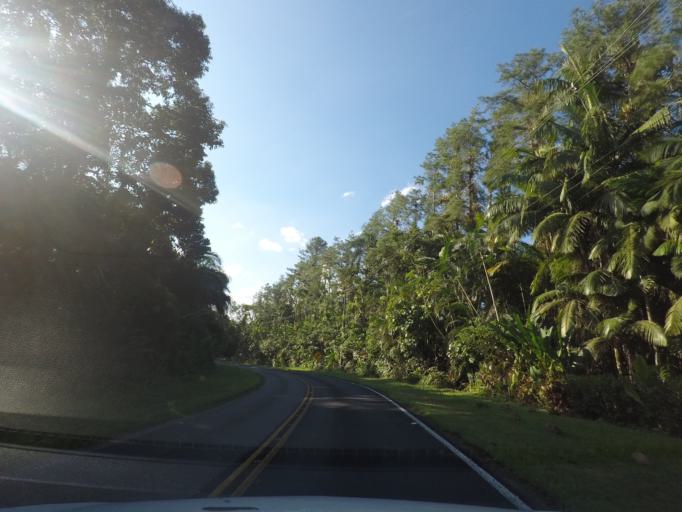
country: BR
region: Parana
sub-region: Antonina
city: Antonina
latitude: -25.4185
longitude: -48.8738
